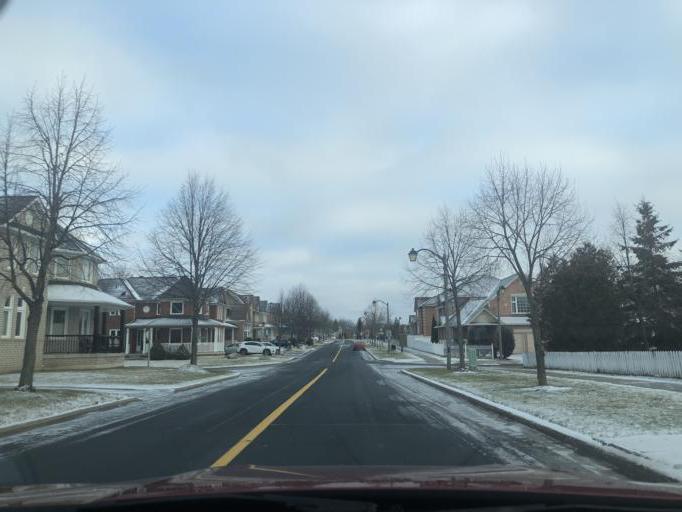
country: CA
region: Ontario
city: Markham
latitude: 43.8659
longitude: -79.2363
